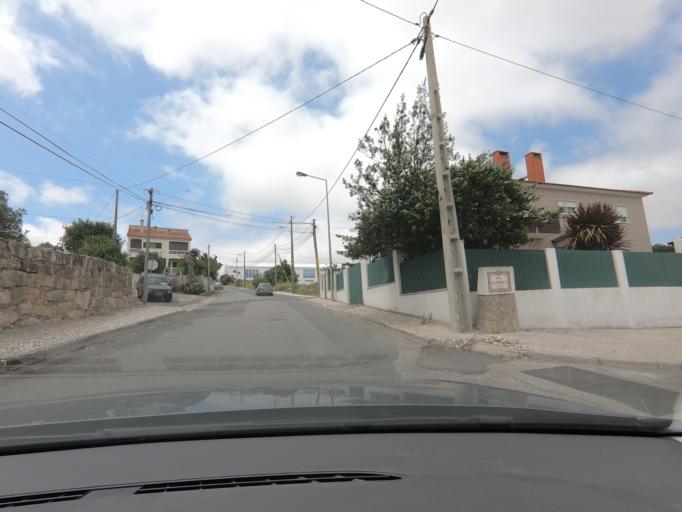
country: PT
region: Lisbon
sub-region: Oeiras
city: Porto Salvo
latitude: 38.7408
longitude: -9.3147
